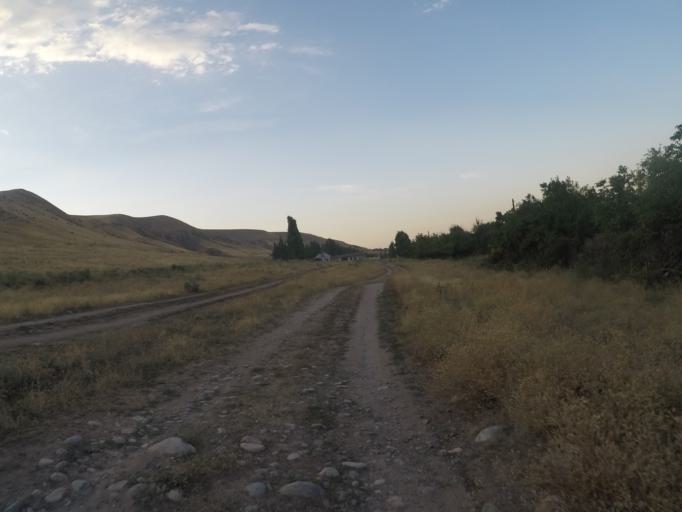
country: KG
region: Chuy
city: Bishkek
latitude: 42.7708
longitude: 74.6394
